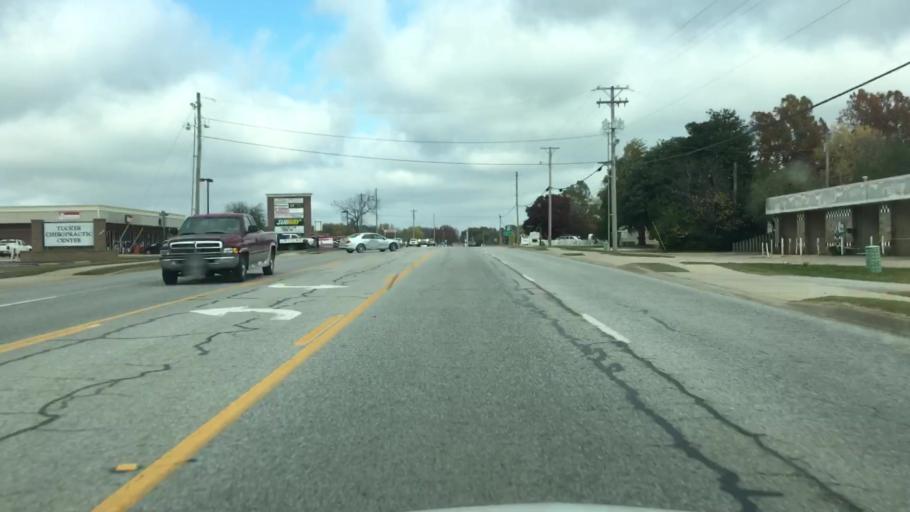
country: US
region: Arkansas
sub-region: Benton County
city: Gentry
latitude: 36.2566
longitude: -94.4852
